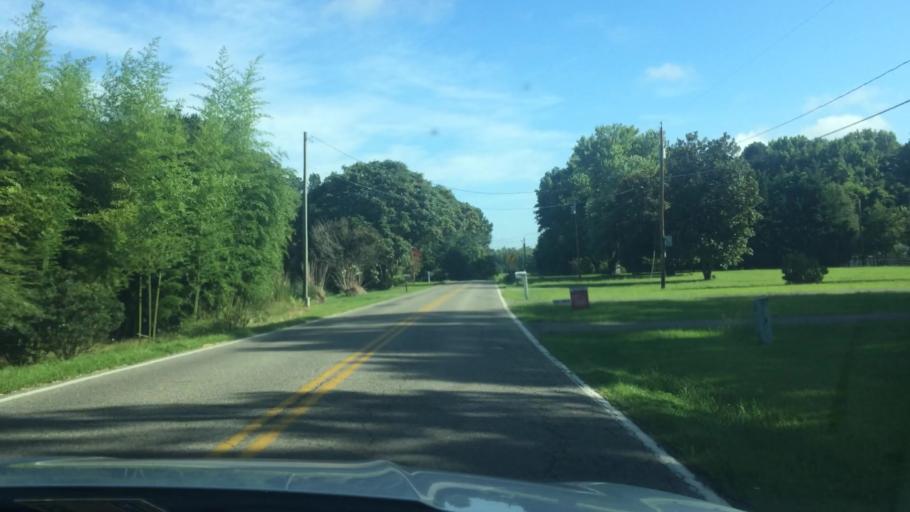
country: US
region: Virginia
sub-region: Middlesex County
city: Deltaville
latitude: 37.5795
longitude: -76.4567
